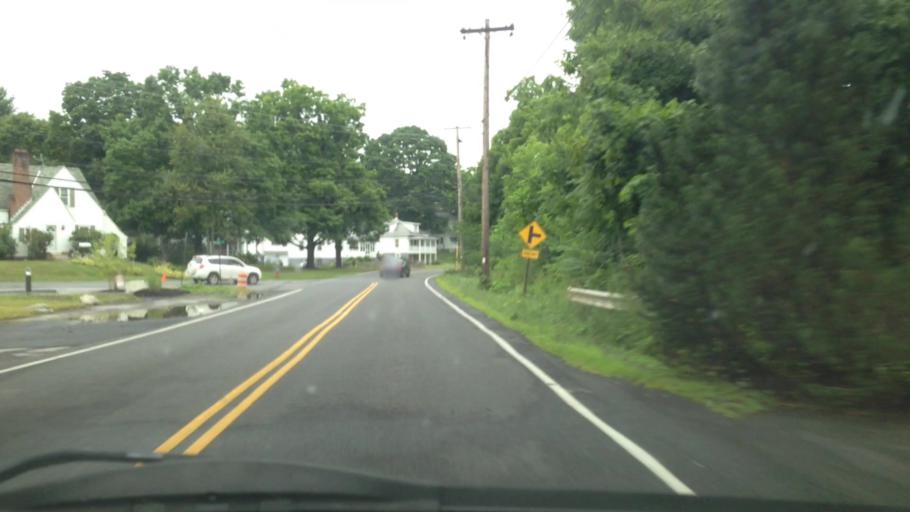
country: US
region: New York
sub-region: Ulster County
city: Highland
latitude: 41.7246
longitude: -73.9677
